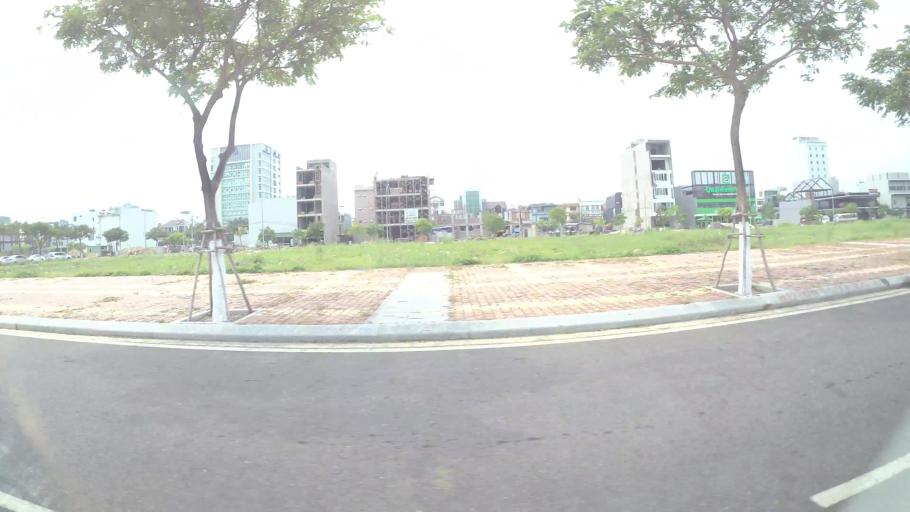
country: VN
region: Da Nang
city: Son Tra
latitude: 16.0561
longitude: 108.2237
